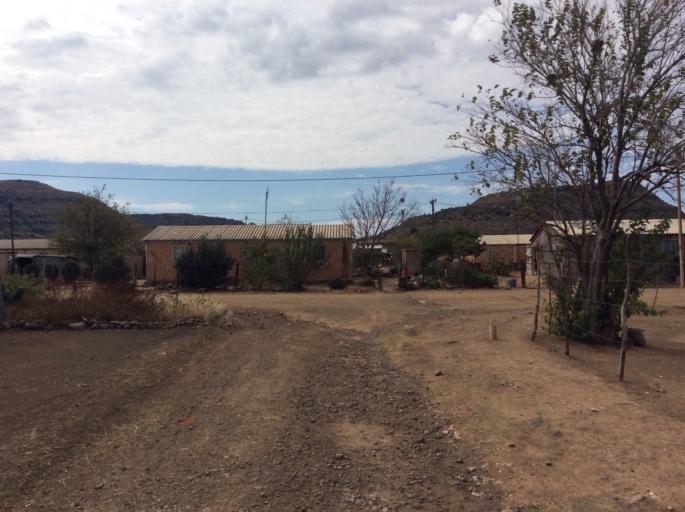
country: LS
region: Mafeteng
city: Mafeteng
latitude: -29.7176
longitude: 27.0275
